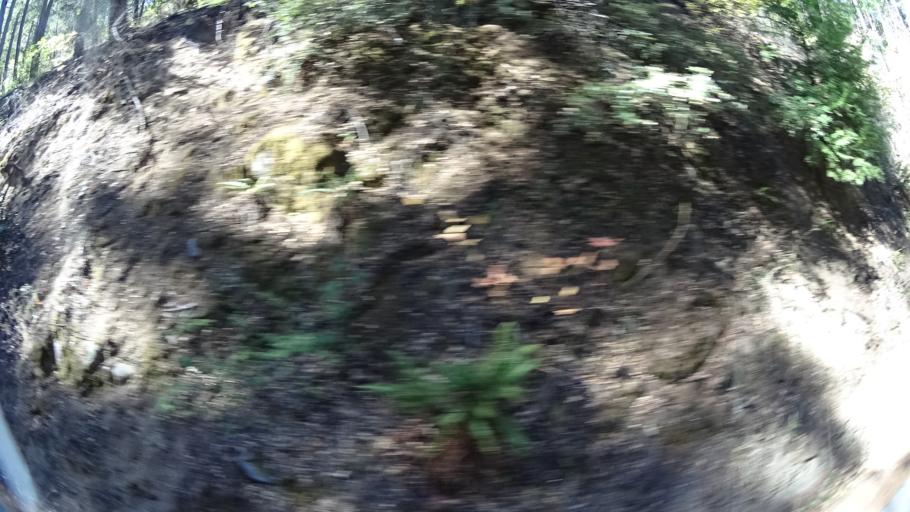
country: US
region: California
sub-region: Siskiyou County
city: Happy Camp
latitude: 41.2920
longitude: -123.2450
